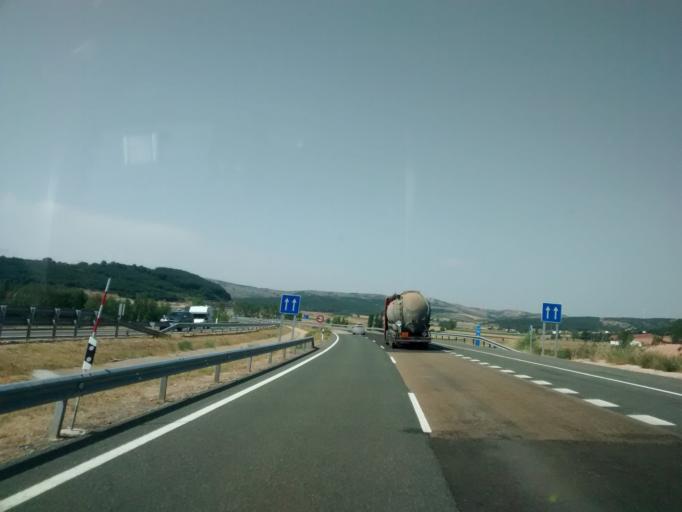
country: ES
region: Castille and Leon
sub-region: Provincia de Palencia
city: Aguilar de Campoo
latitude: 42.7687
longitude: -4.2780
